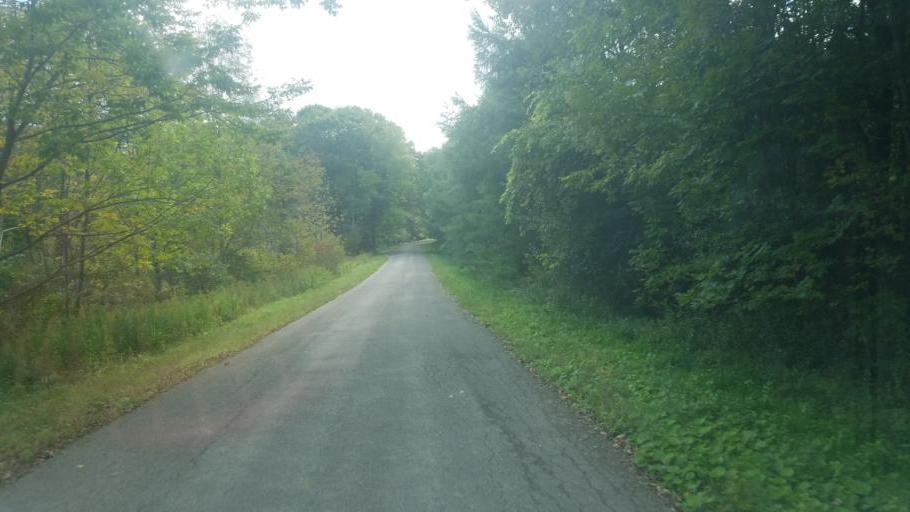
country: US
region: New York
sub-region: Allegany County
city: Cuba
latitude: 42.2277
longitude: -78.3515
